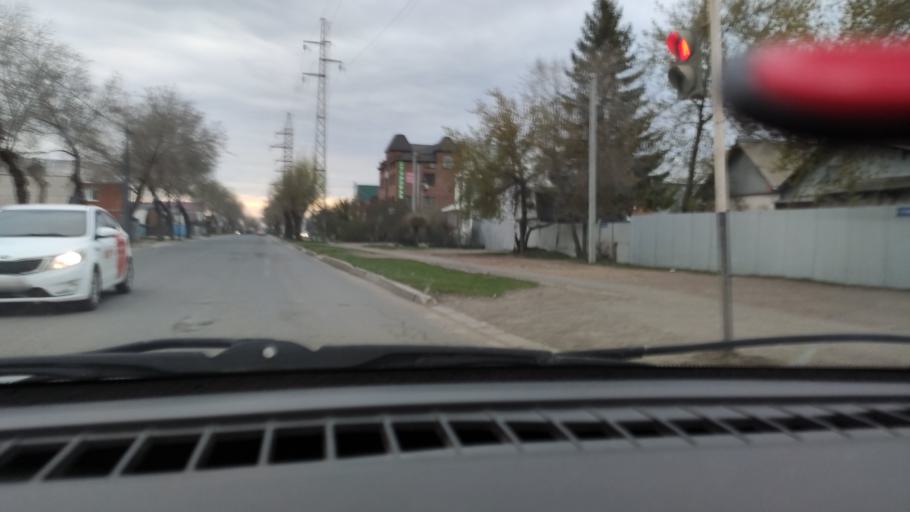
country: RU
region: Orenburg
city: Orenburg
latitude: 51.7756
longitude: 55.1179
